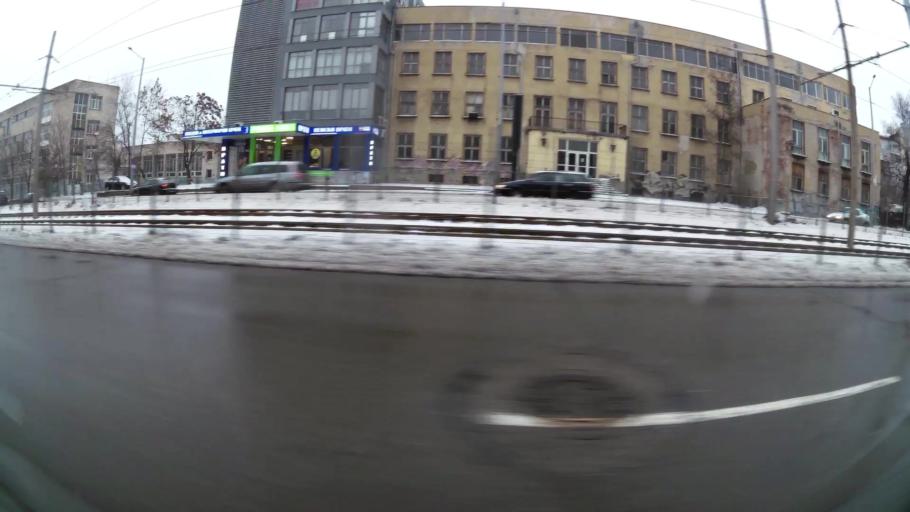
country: BG
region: Sofia-Capital
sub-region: Stolichna Obshtina
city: Sofia
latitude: 42.6943
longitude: 23.3550
